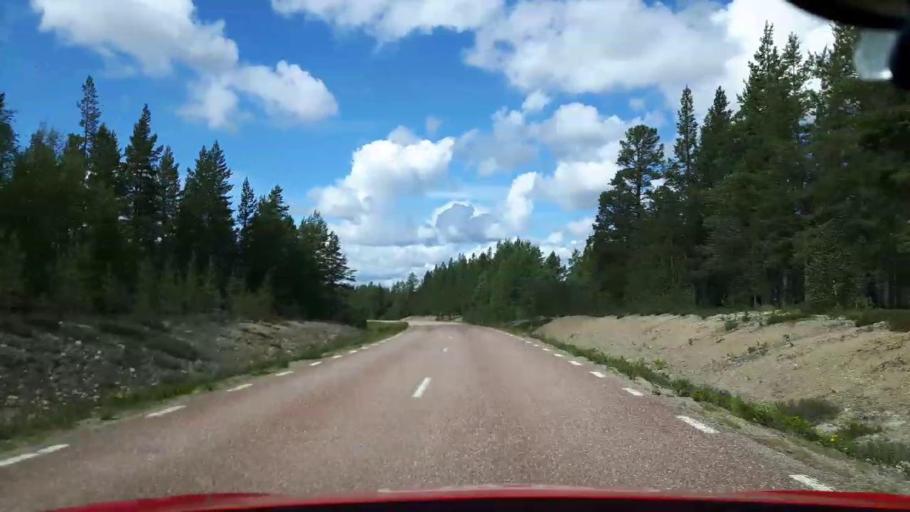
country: SE
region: Dalarna
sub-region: Alvdalens Kommun
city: AElvdalen
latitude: 61.8047
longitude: 13.6539
